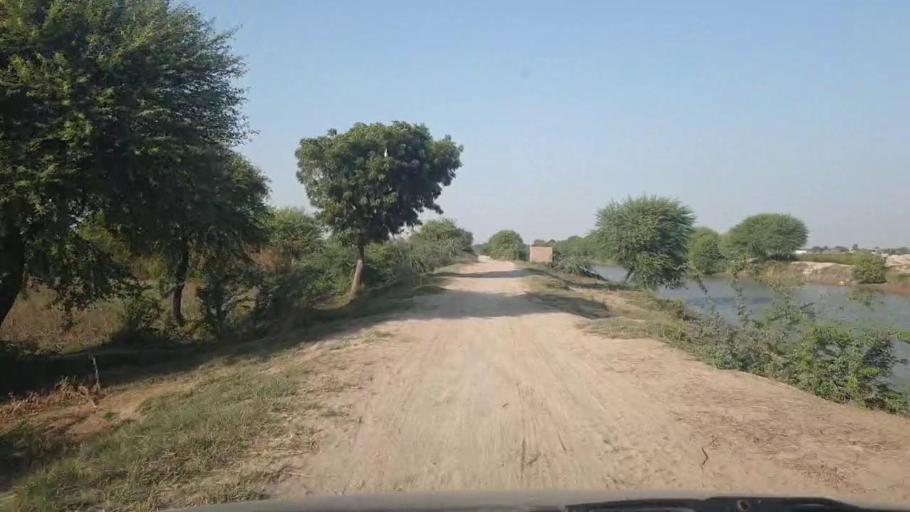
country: PK
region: Sindh
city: Badin
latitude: 24.6449
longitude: 68.8151
